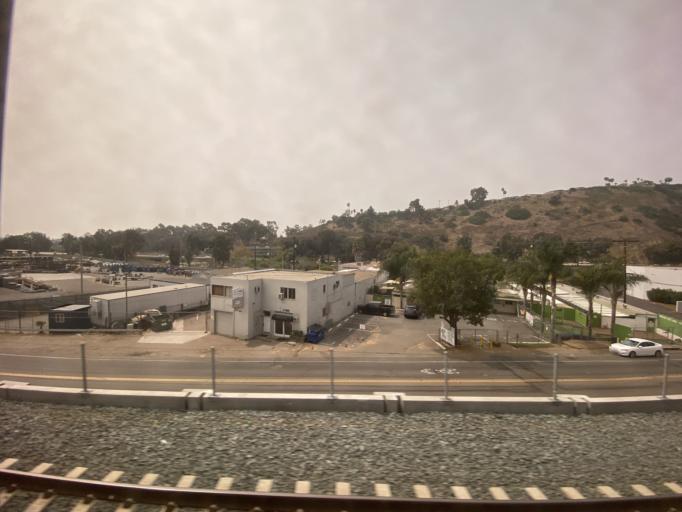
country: US
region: California
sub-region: San Diego County
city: La Jolla
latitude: 32.8136
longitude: -117.2187
